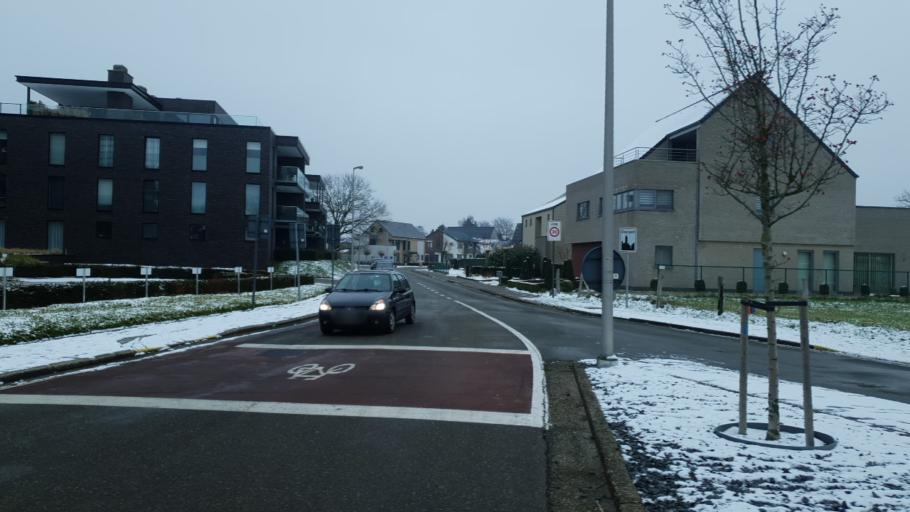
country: BE
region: Flanders
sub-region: Provincie Limburg
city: Overpelt
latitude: 51.2072
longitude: 5.4225
